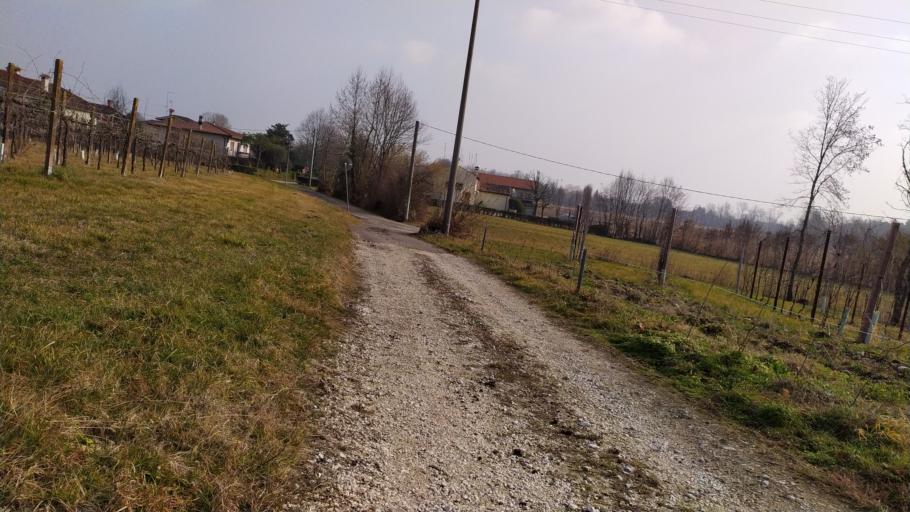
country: IT
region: Veneto
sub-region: Provincia di Treviso
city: San Fior di Sopra
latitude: 45.9306
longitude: 12.3518
